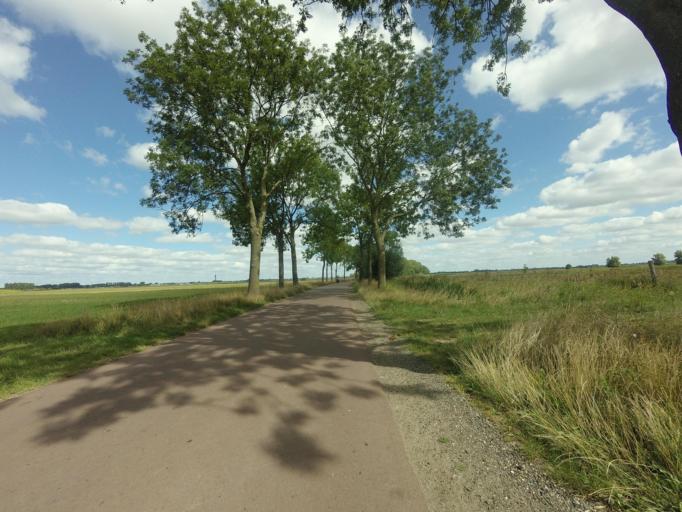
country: NL
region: North Brabant
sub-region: Gemeente Oss
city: Berghem
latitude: 51.7814
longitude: 5.5972
